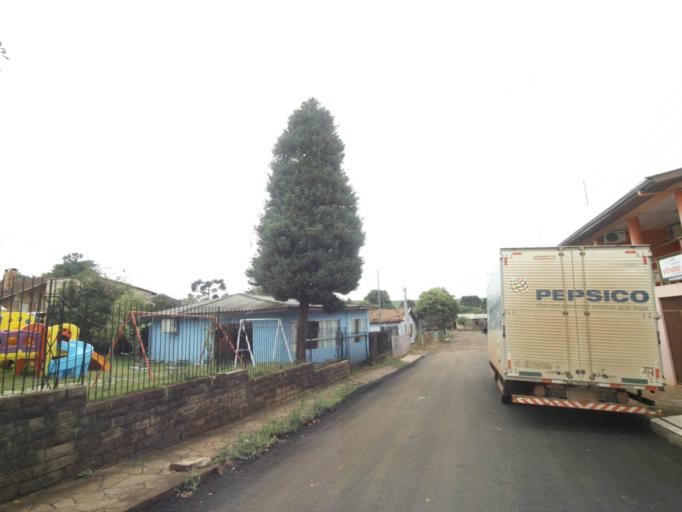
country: BR
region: Rio Grande do Sul
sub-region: Lagoa Vermelha
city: Lagoa Vermelha
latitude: -28.2210
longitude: -51.5225
